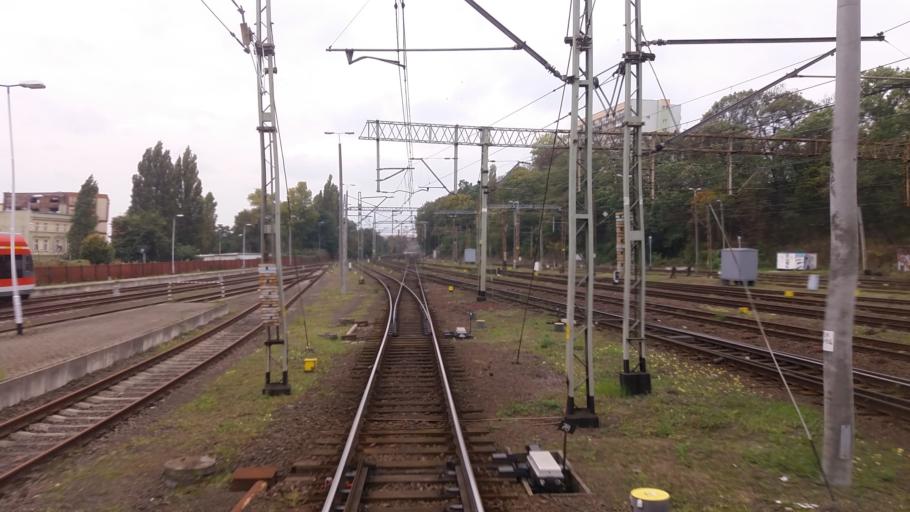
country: PL
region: West Pomeranian Voivodeship
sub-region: Szczecin
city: Szczecin
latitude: 53.4155
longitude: 14.5458
